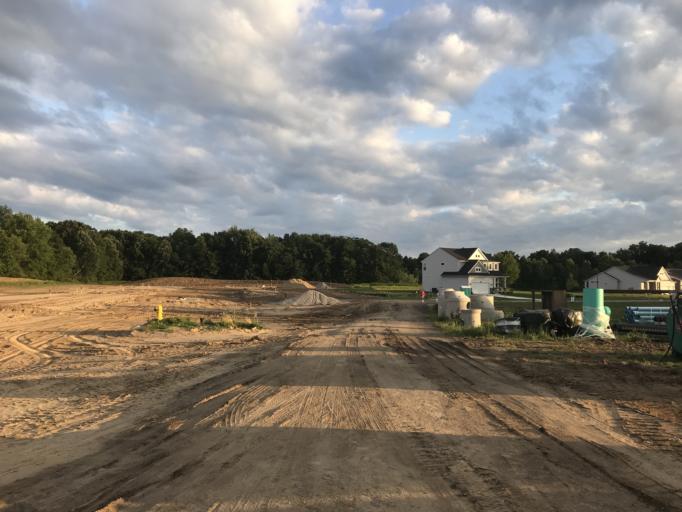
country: US
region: Michigan
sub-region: Eaton County
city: Waverly
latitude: 42.7507
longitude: -84.6749
